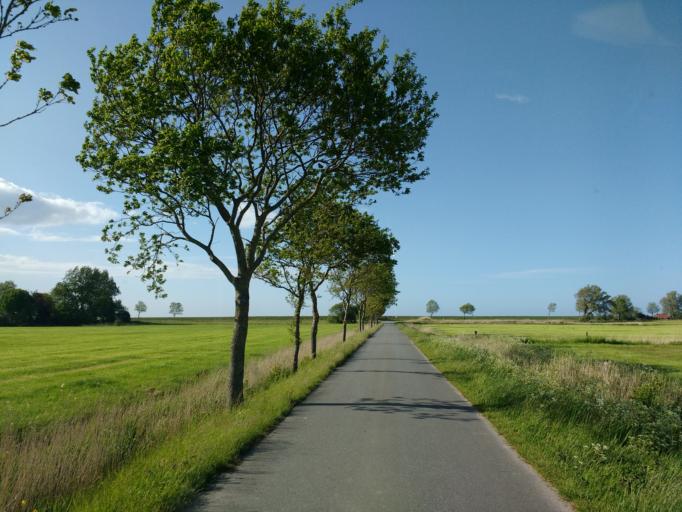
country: DE
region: Lower Saxony
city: Schillig
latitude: 53.7042
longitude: 7.9416
